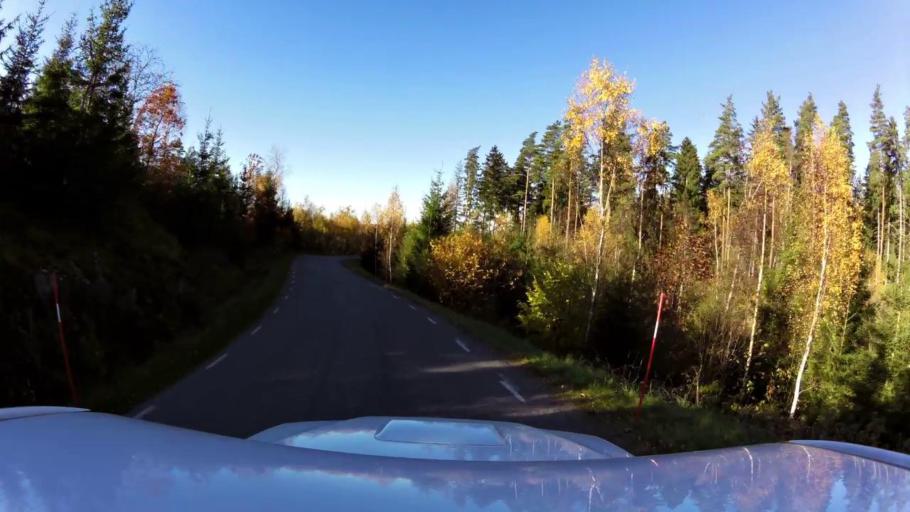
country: SE
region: OEstergoetland
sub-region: Linkopings Kommun
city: Ljungsbro
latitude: 58.5370
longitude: 15.4337
